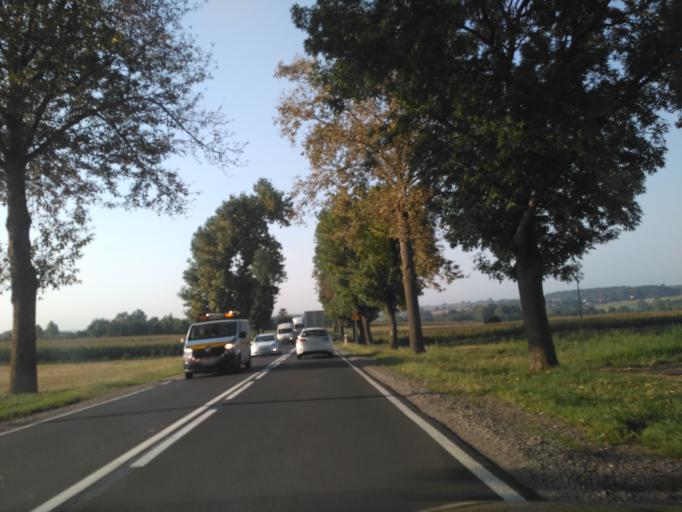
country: PL
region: Lublin Voivodeship
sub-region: Powiat krasnicki
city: Szastarka
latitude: 50.8087
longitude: 22.3196
